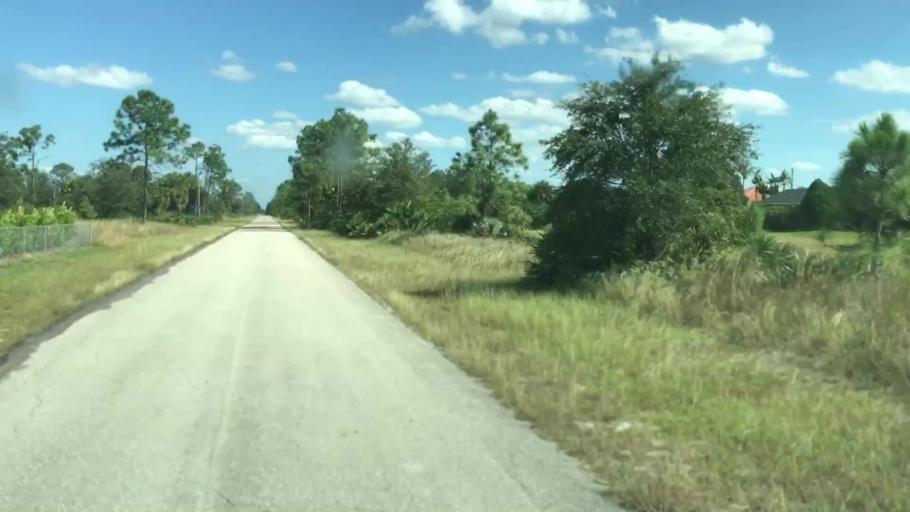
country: US
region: Florida
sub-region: Lee County
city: Lehigh Acres
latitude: 26.6284
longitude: -81.6318
